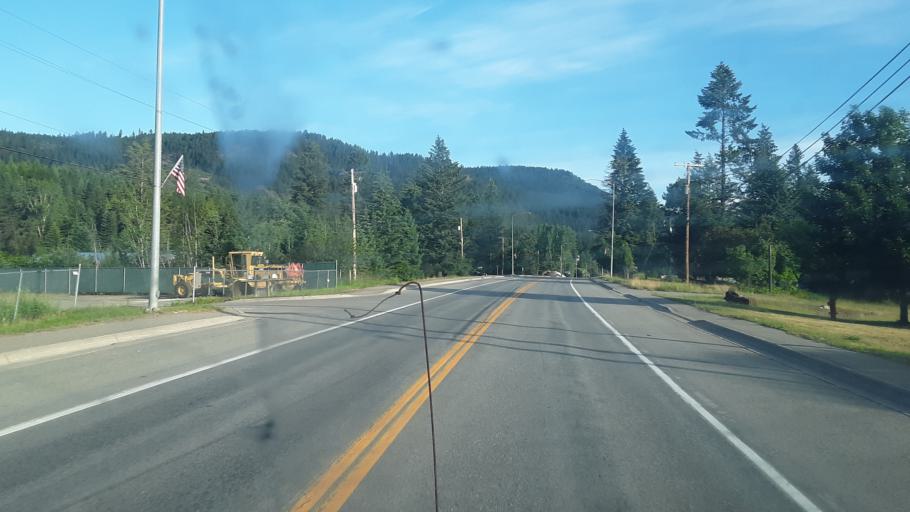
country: US
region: Montana
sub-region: Lincoln County
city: Libby
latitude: 48.4511
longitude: -115.8832
